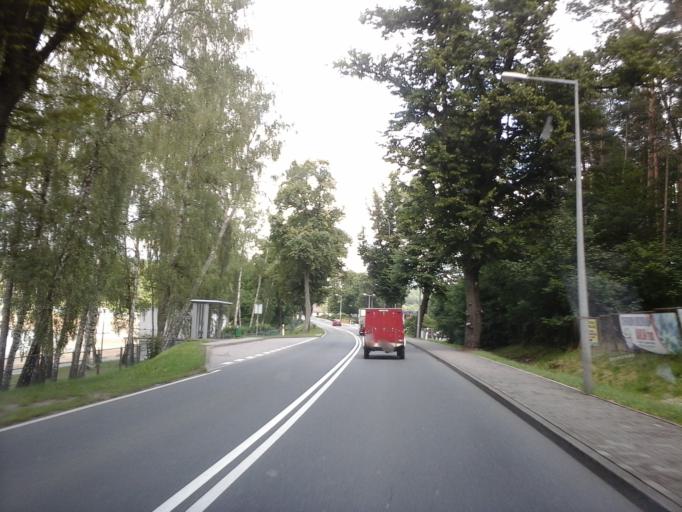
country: PL
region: Lubusz
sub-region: Powiat strzelecko-drezdenecki
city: Stare Kurowo
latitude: 52.9102
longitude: 15.6655
